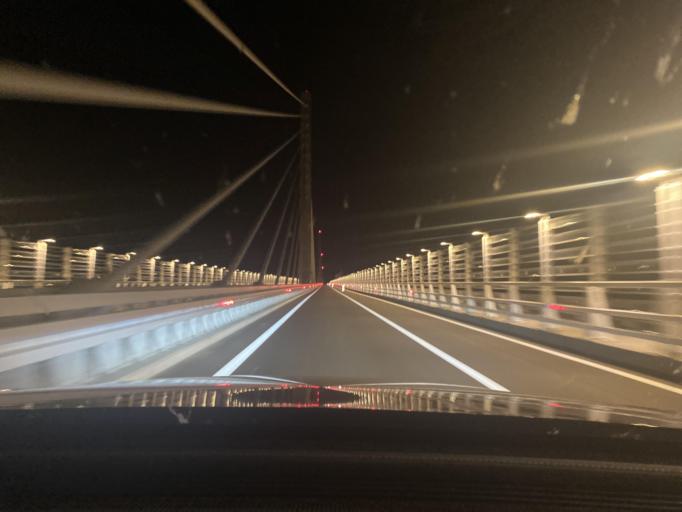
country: BA
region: Federation of Bosnia and Herzegovina
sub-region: Hercegovacko-Bosanski Kanton
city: Neum
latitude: 42.9379
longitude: 17.5419
